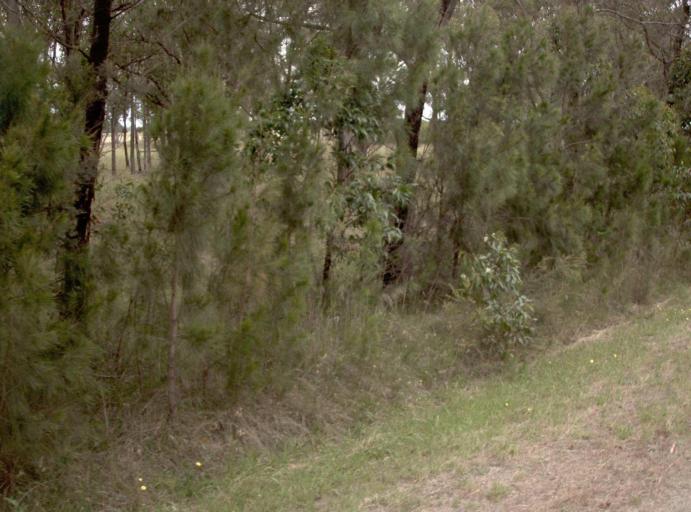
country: AU
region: Victoria
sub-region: Latrobe
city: Traralgon
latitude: -38.4791
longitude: 146.8214
